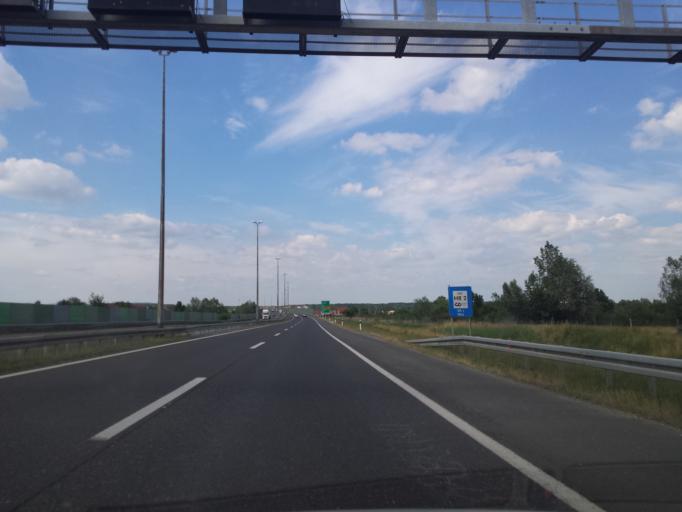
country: HR
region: Grad Zagreb
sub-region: Sesvete
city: Sesvete
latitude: 45.8104
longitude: 16.1348
